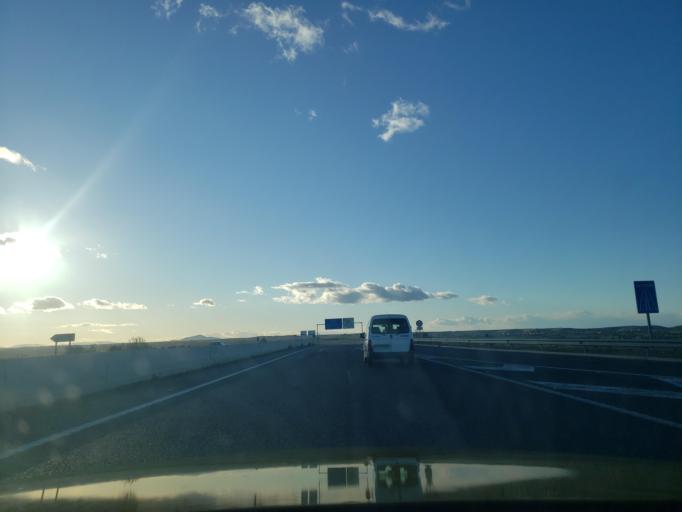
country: ES
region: Castille-La Mancha
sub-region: Province of Toledo
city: Burguillos de Toledo
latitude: 39.8168
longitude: -3.9812
